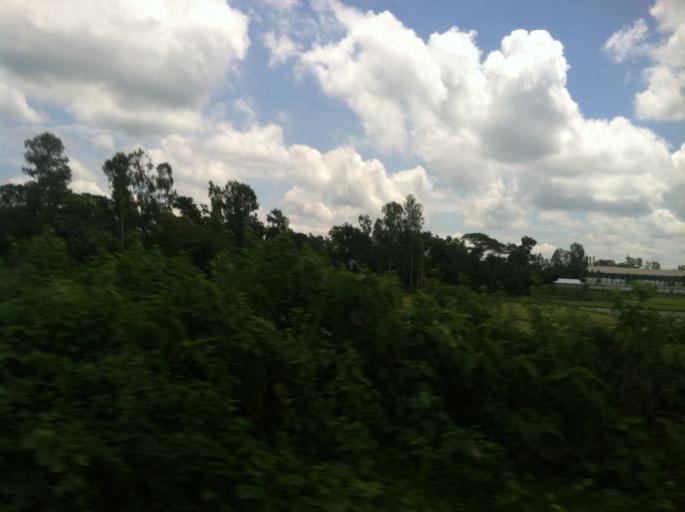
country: BD
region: Sylhet
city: Habiganj
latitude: 24.1861
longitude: 91.3507
